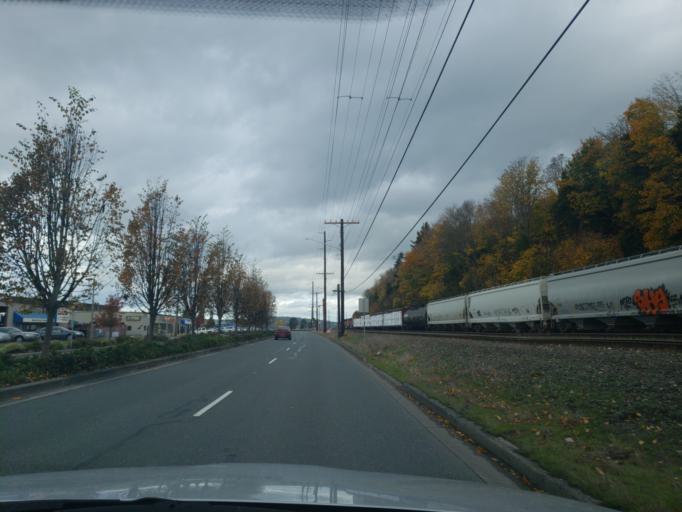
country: US
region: Washington
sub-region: Snohomish County
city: Everett
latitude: 48.0023
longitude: -122.2138
